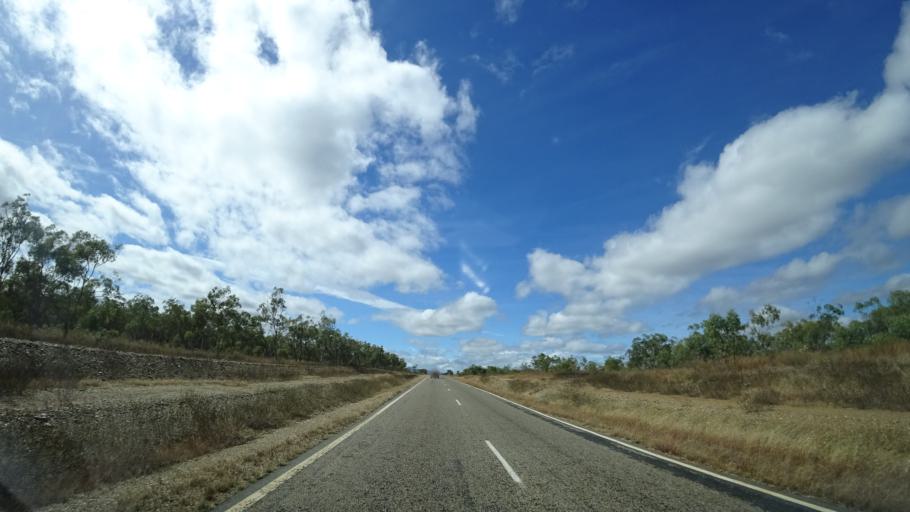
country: AU
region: Queensland
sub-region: Cairns
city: Port Douglas
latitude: -16.4957
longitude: 144.9679
